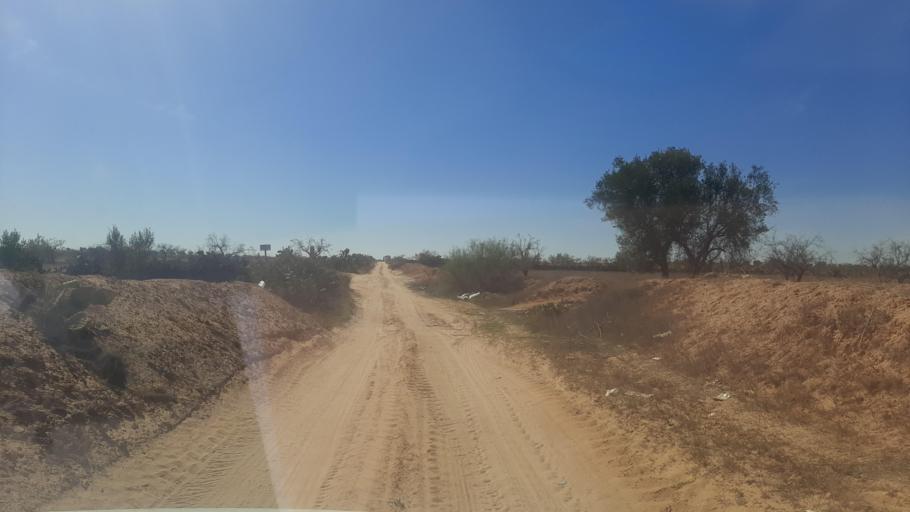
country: TN
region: Safaqis
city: Sfax
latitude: 34.8390
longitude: 10.5589
